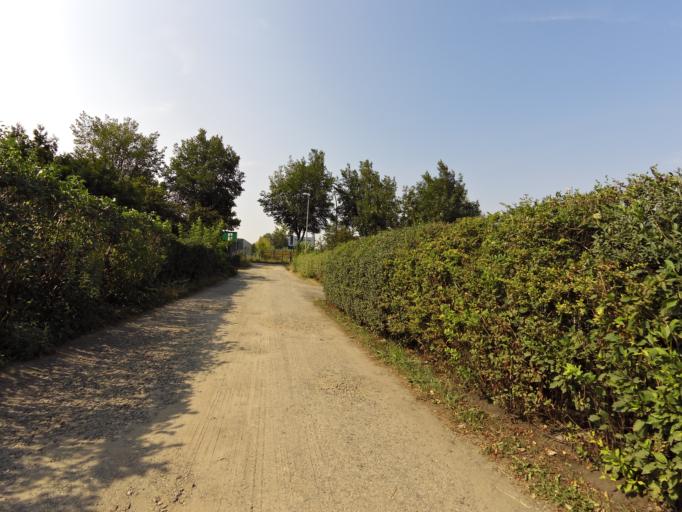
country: DE
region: Berlin
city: Adlershof
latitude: 52.4273
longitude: 13.5491
